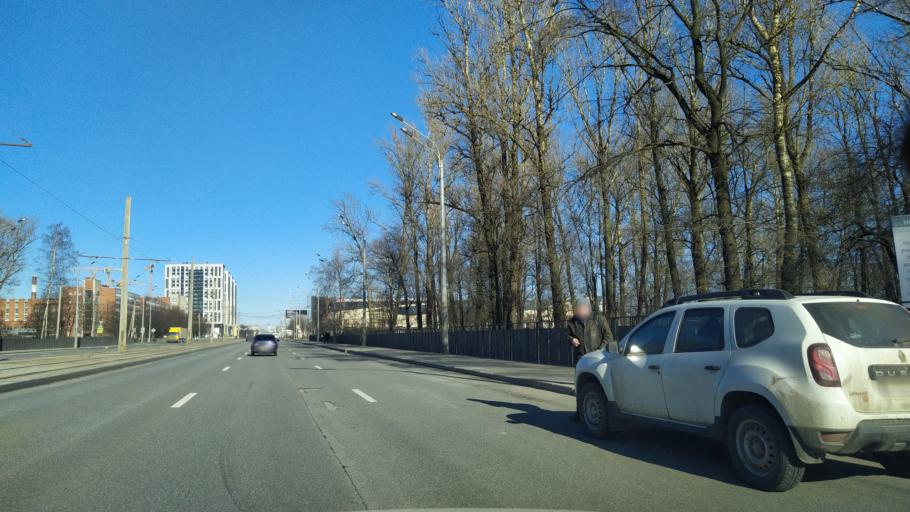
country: RU
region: St.-Petersburg
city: Kupchino
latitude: 59.8811
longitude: 30.3606
